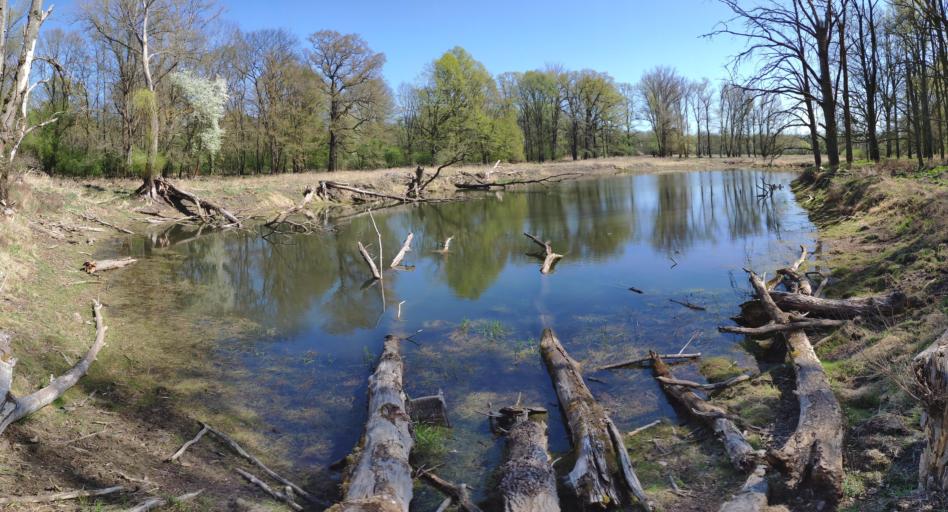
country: PL
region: Lubusz
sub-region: Powiat zielonogorski
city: Zabor
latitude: 51.9854
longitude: 15.6814
